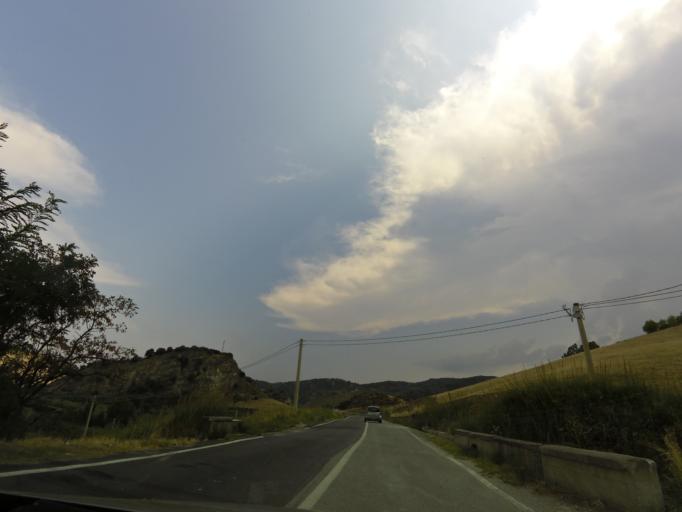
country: IT
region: Calabria
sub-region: Provincia di Reggio Calabria
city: Stilo
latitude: 38.4767
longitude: 16.4791
